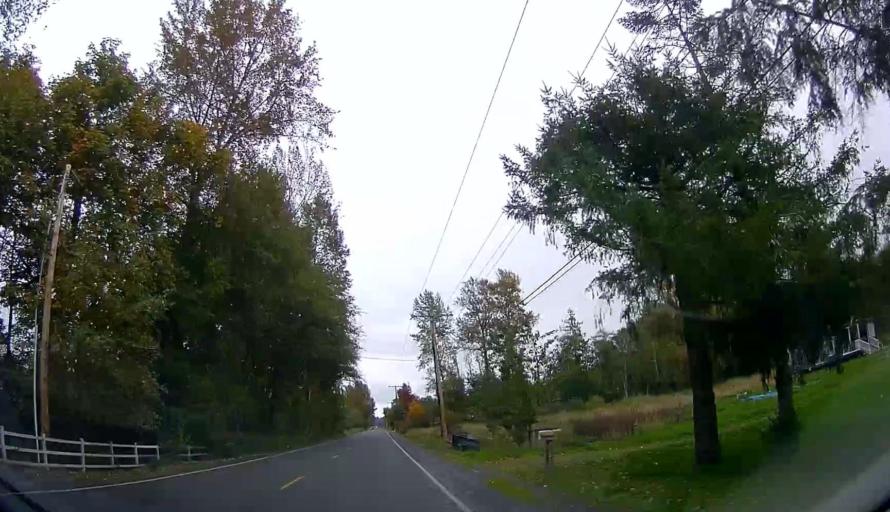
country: US
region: Washington
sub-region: Skagit County
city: Sedro-Woolley
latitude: 48.5241
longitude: -122.1631
